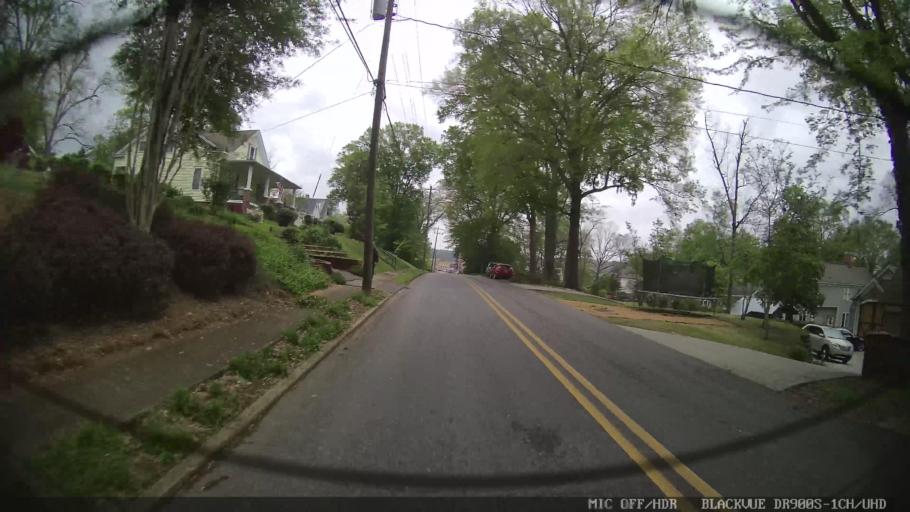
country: US
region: Georgia
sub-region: Bartow County
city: Cartersville
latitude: 34.1661
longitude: -84.8029
